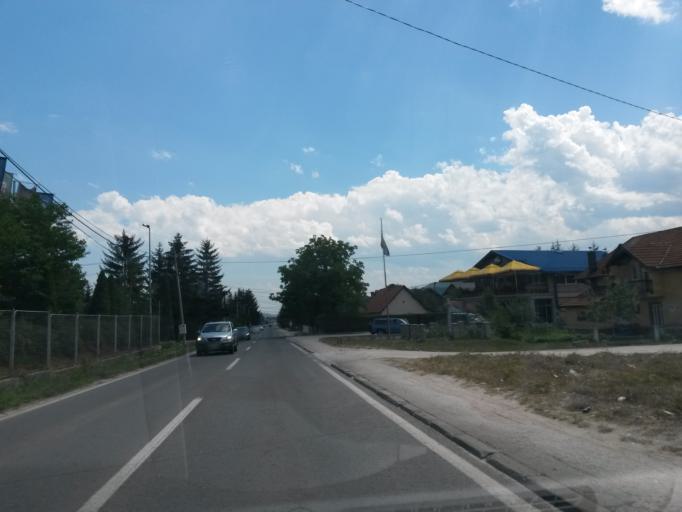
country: BA
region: Federation of Bosnia and Herzegovina
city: Travnik
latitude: 44.2099
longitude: 17.7109
